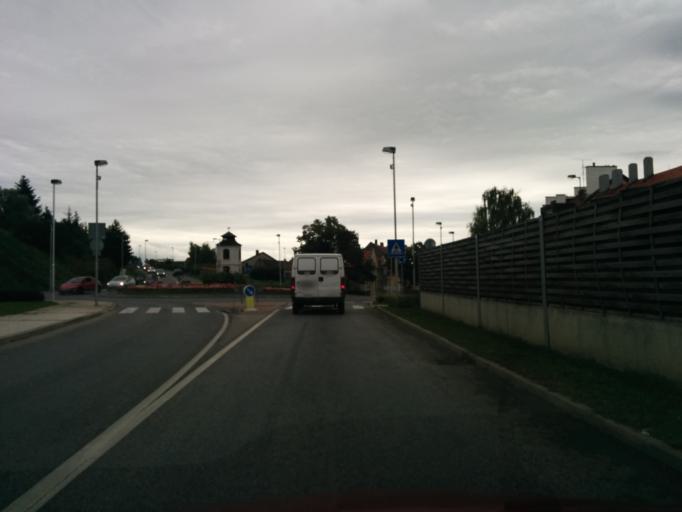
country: HU
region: Gyor-Moson-Sopron
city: Sopron
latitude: 47.6918
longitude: 16.5896
